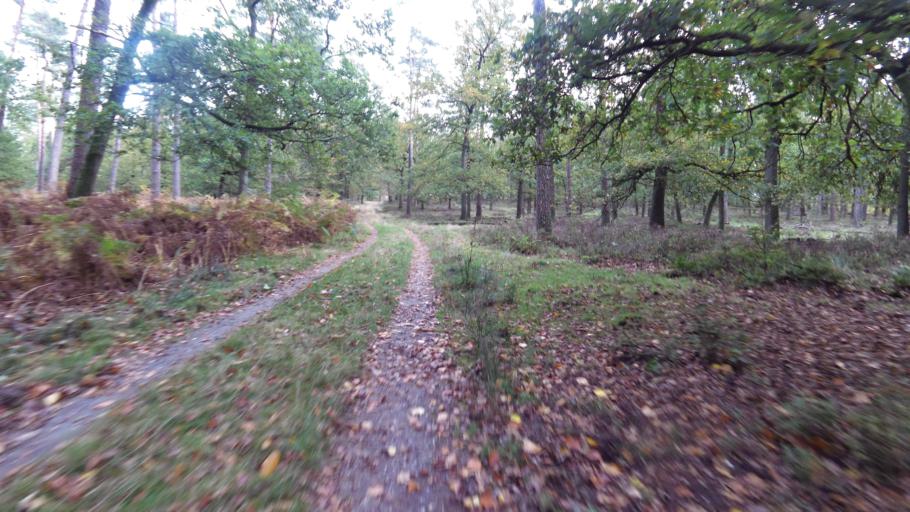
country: NL
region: Gelderland
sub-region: Gemeente Epe
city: Vaassen
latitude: 52.3202
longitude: 5.8717
